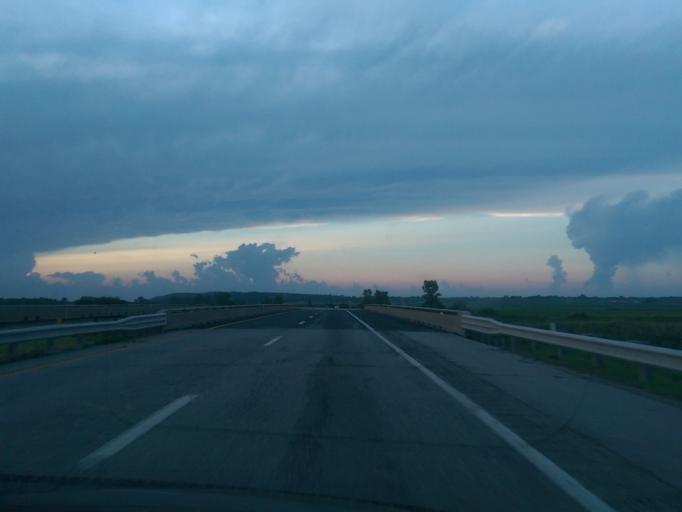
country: US
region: Iowa
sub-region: Fremont County
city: Hamburg
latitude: 40.5119
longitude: -95.6018
